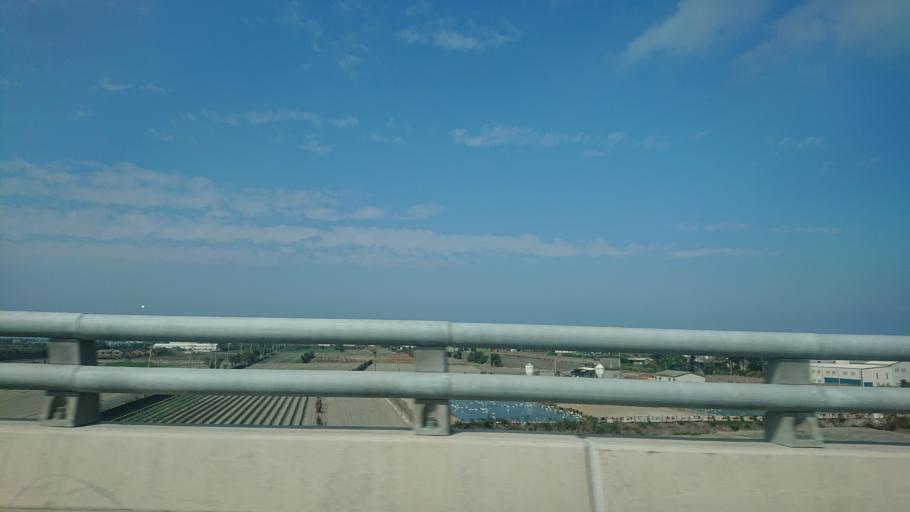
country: TW
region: Taiwan
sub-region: Changhua
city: Chang-hua
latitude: 23.9960
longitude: 120.3783
